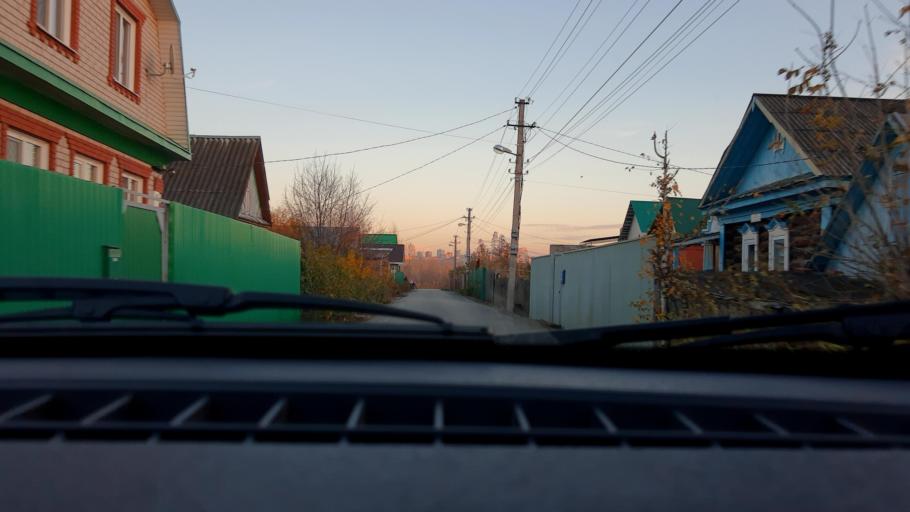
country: RU
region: Bashkortostan
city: Mikhaylovka
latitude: 54.7584
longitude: 55.9080
